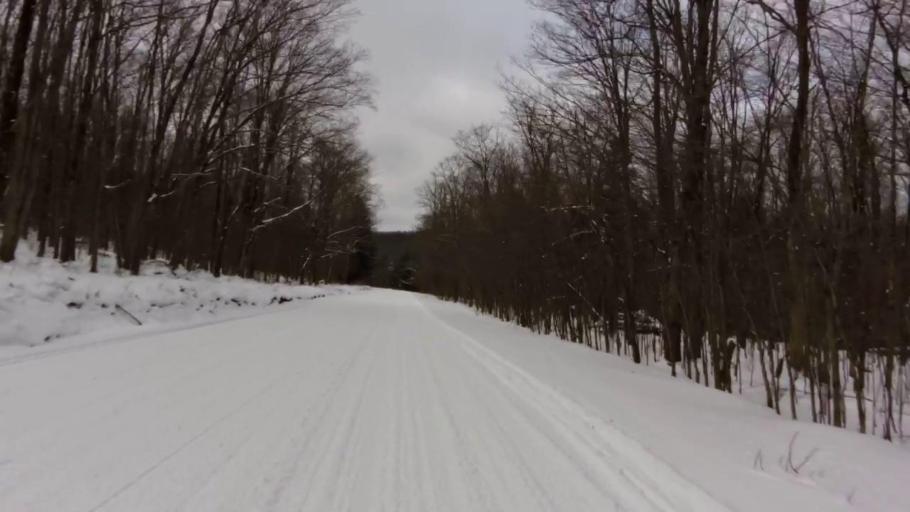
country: US
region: New York
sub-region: Cattaraugus County
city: Salamanca
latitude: 42.0344
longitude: -78.7995
